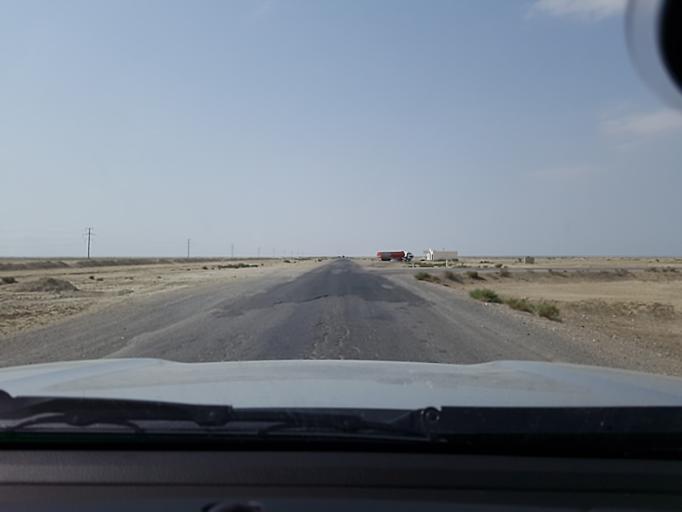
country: TM
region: Balkan
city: Gumdag
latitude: 38.9979
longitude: 54.5864
